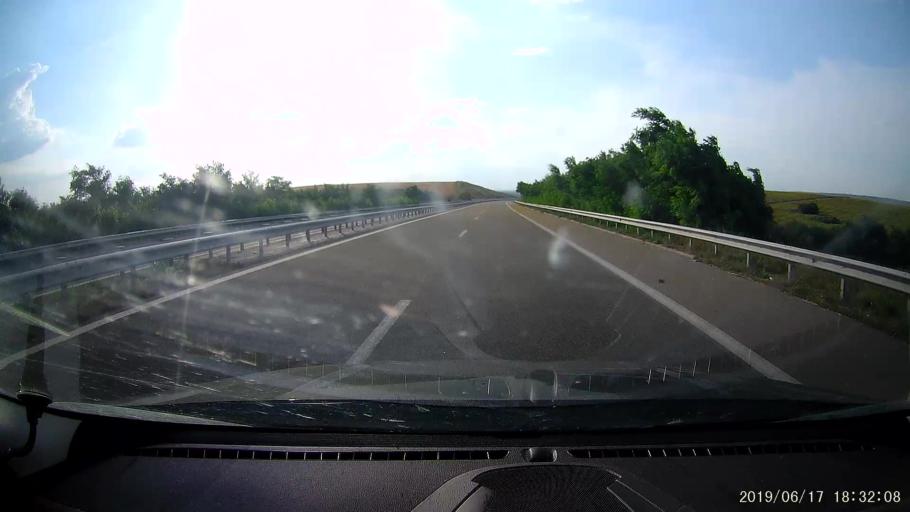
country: BG
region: Khaskovo
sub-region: Obshtina Dimitrovgrad
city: Dimitrovgrad
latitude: 42.0550
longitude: 25.4866
